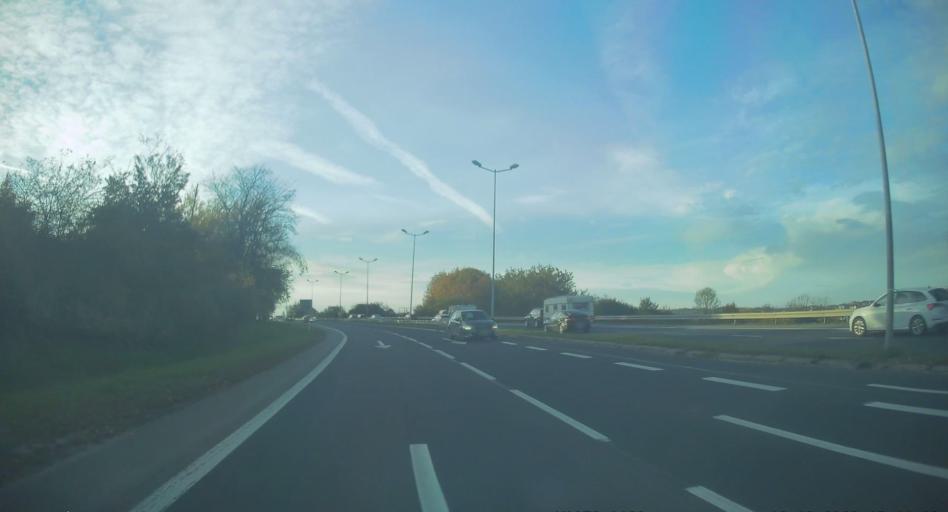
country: PL
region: Lesser Poland Voivodeship
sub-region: Powiat olkuski
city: Olkusz
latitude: 50.2787
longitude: 19.5777
